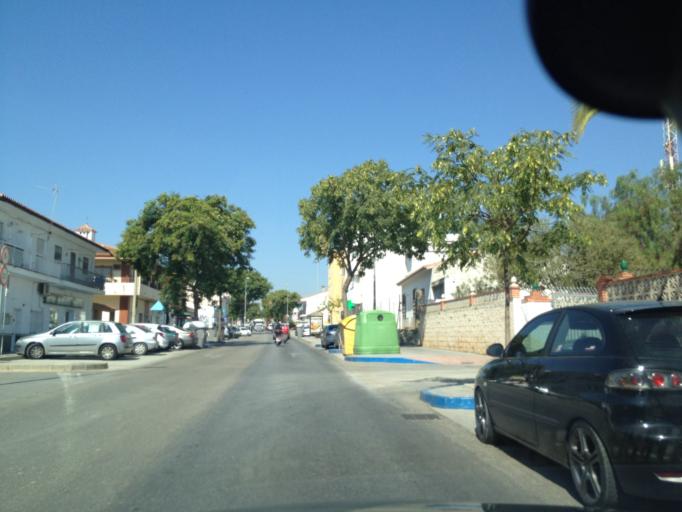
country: ES
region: Andalusia
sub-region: Provincia de Malaga
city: Alhaurin de la Torre
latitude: 36.7266
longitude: -4.5426
